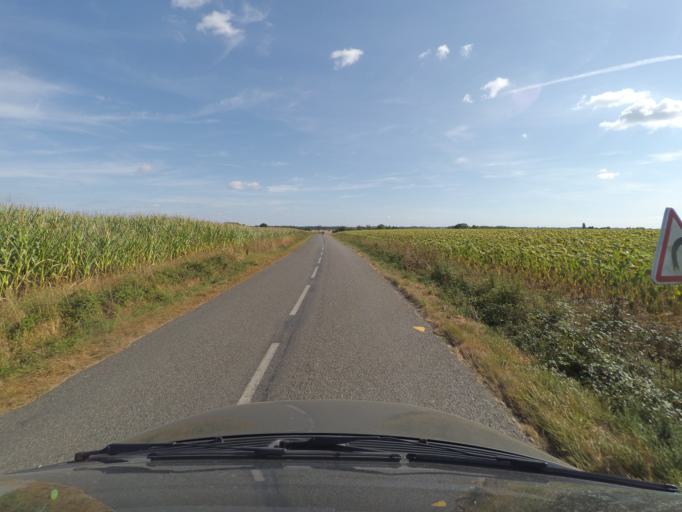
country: FR
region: Pays de la Loire
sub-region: Departement de la Loire-Atlantique
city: Montbert
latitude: 47.0695
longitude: -1.4709
